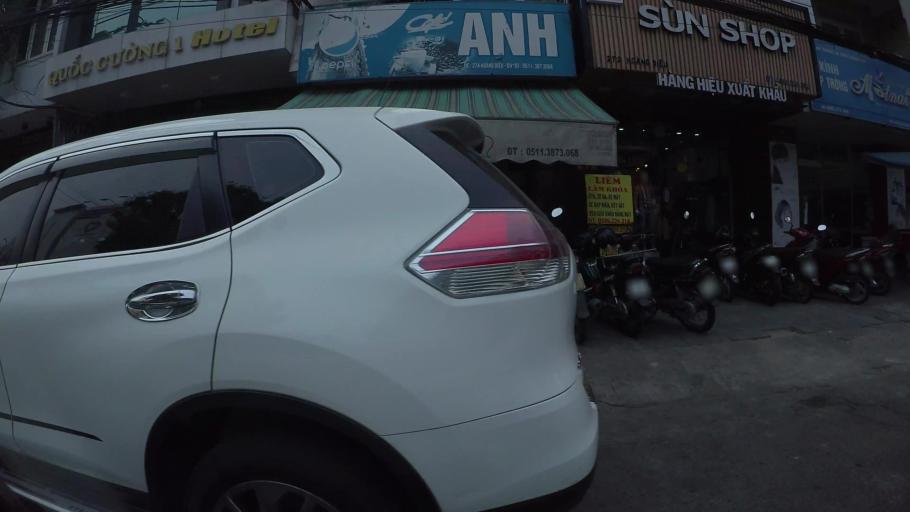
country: VN
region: Da Nang
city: Da Nang
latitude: 16.0593
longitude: 108.2170
